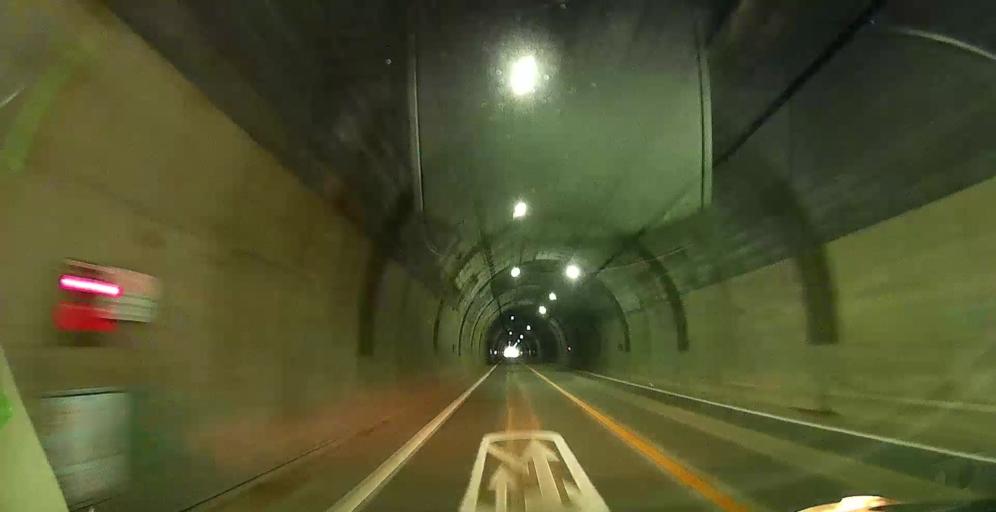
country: JP
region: Kumamoto
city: Minamata
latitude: 32.2460
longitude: 130.4885
